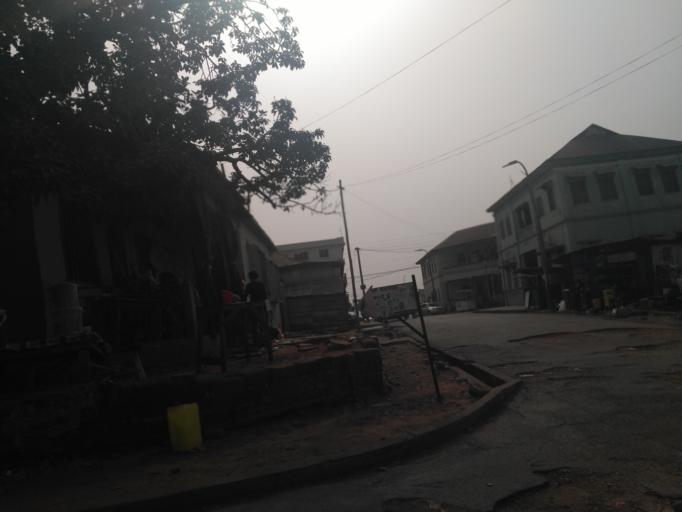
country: GH
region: Ashanti
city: Kumasi
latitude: 6.7034
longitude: -1.6325
